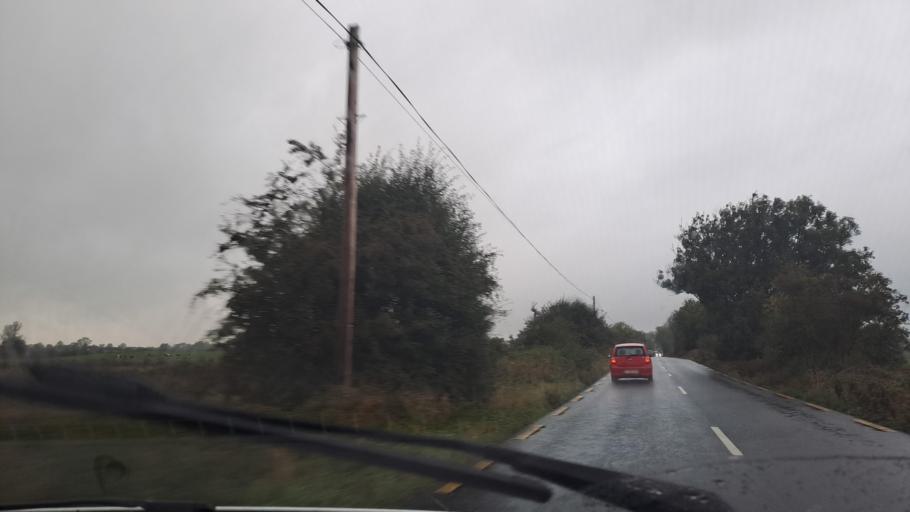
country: GB
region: Northern Ireland
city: Crossmaglen
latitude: 53.9707
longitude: -6.5867
